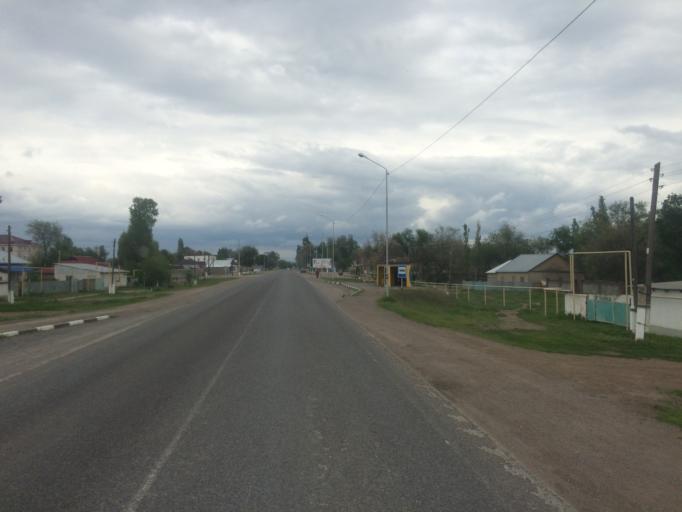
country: KZ
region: Zhambyl
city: Georgiyevka
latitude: 43.2276
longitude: 74.3905
